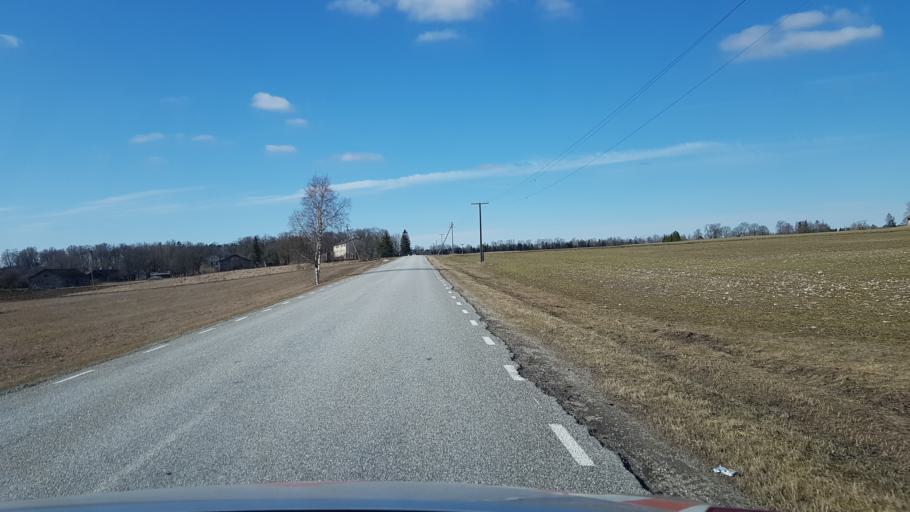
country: EE
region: Laeaene-Virumaa
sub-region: Tapa vald
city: Tapa
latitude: 59.2690
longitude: 26.0100
